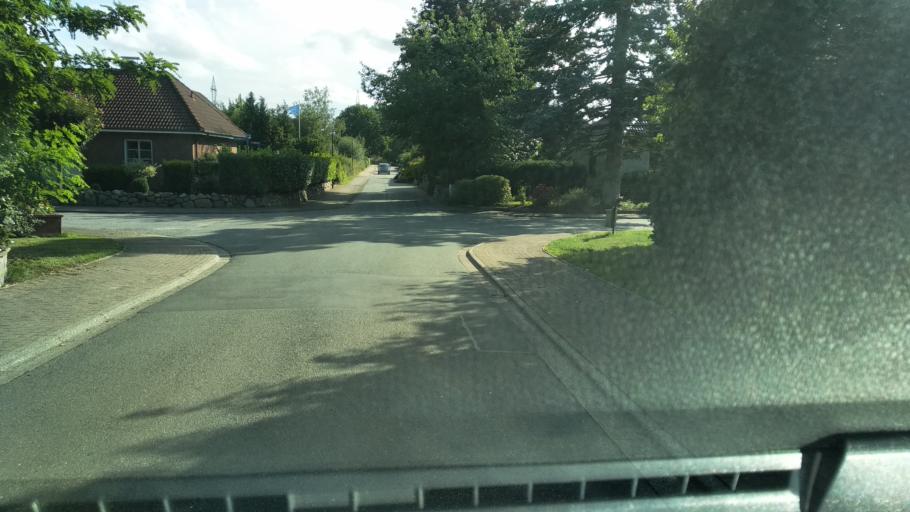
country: DE
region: Schleswig-Holstein
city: Busdorf
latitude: 54.4871
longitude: 9.5451
